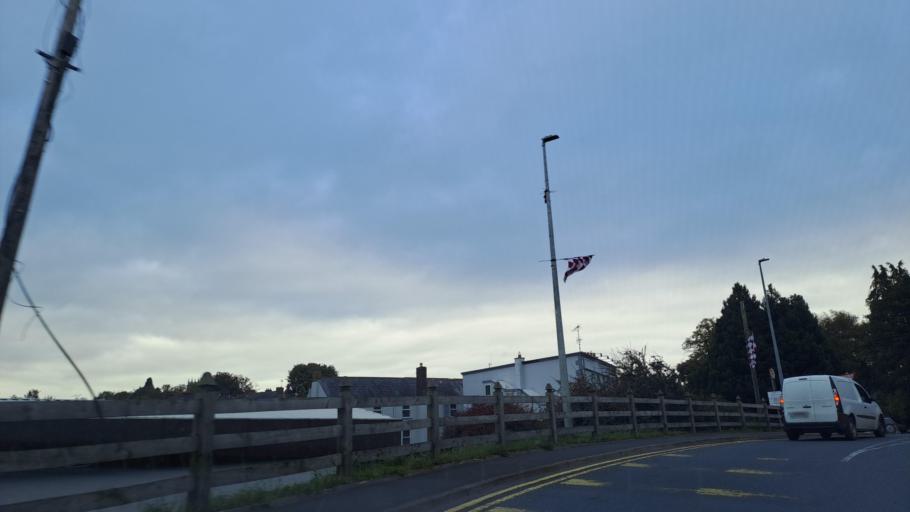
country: IE
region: Ulster
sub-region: County Monaghan
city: Monaghan
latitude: 54.1247
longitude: -6.9016
